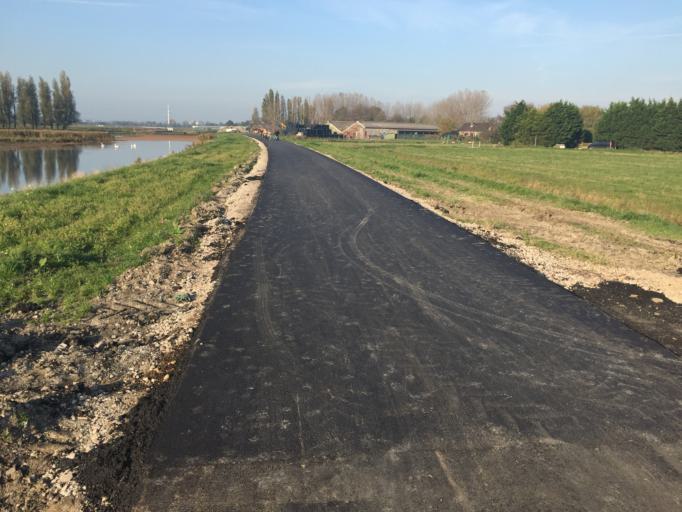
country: NL
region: South Holland
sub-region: Gemeente Lansingerland
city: Berkel en Rodenrijs
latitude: 52.0183
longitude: 4.4807
